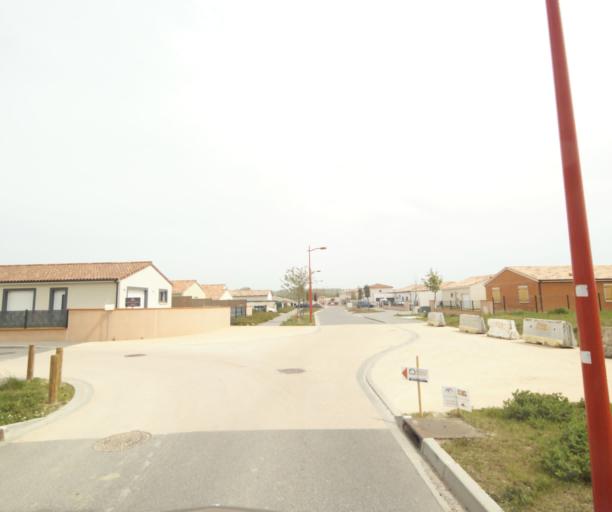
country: FR
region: Midi-Pyrenees
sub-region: Departement de la Haute-Garonne
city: Pompertuzat
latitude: 43.4991
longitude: 1.5175
